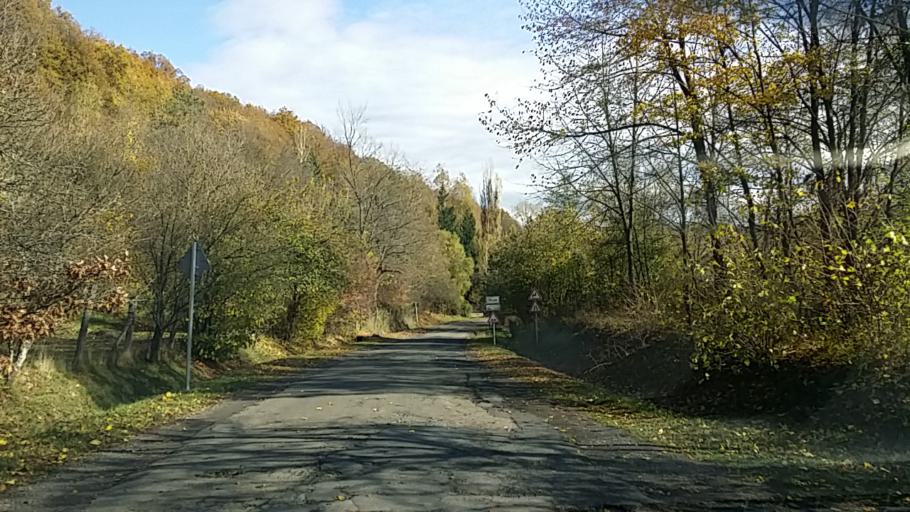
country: HU
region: Borsod-Abauj-Zemplen
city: Tolcsva
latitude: 48.3798
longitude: 21.3921
